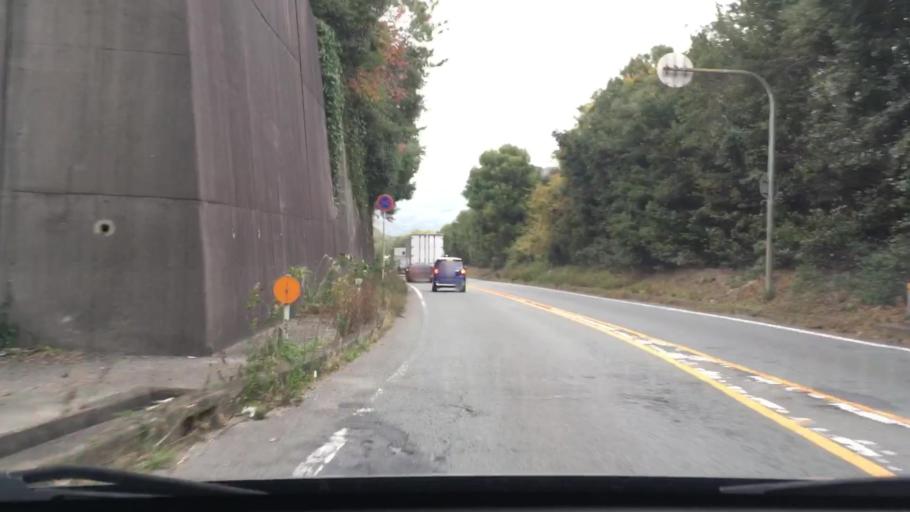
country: JP
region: Yamaguchi
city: Hofu
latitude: 34.0589
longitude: 131.6140
